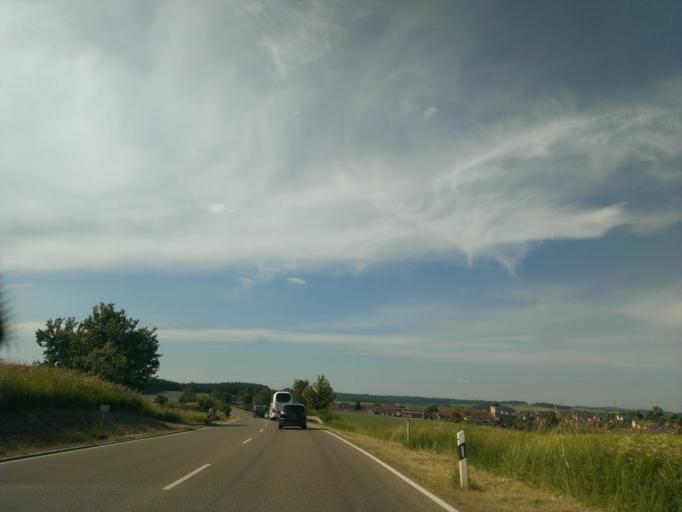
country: DE
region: Bavaria
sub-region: Swabia
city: Marktoffingen
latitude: 48.9380
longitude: 10.4617
